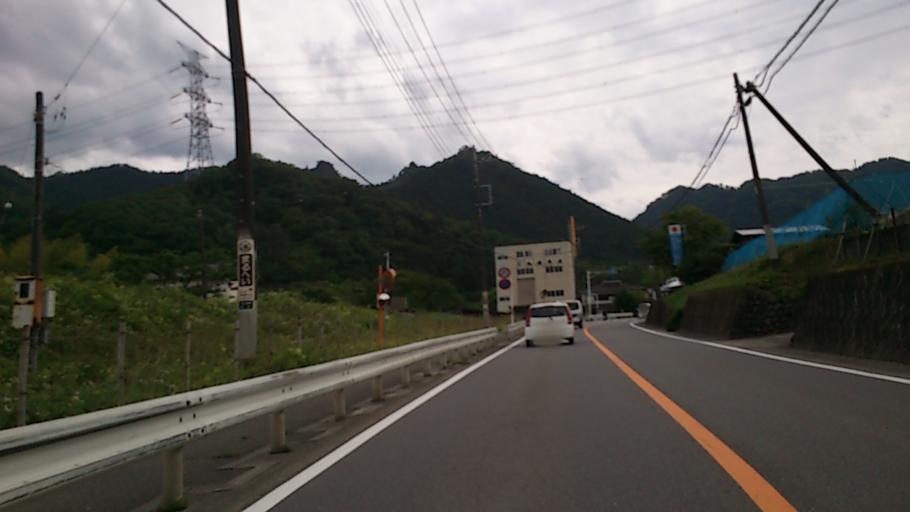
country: JP
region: Gunma
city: Tomioka
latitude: 36.2148
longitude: 138.8032
